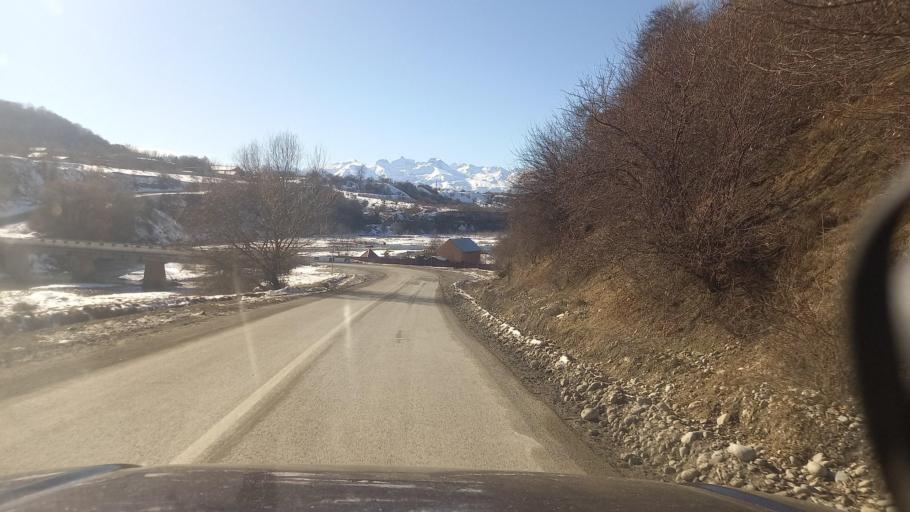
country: RU
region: North Ossetia
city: Chikola
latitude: 43.2310
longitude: 43.9318
